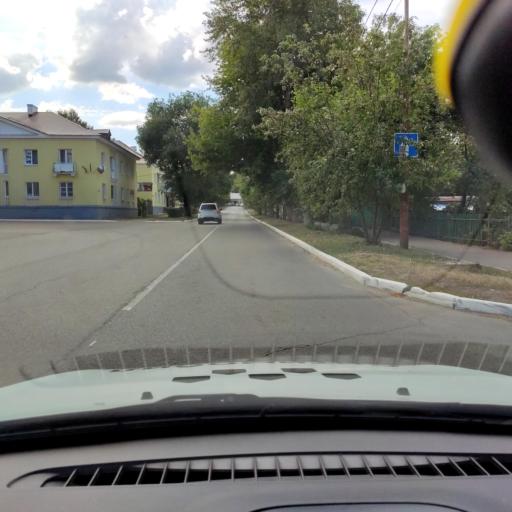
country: RU
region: Samara
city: Zhigulevsk
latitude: 53.4018
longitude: 49.4916
